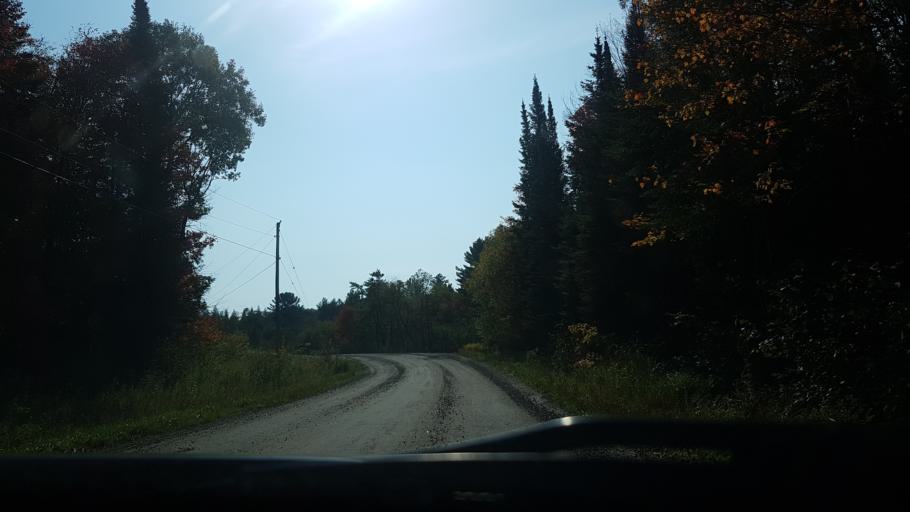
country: CA
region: Ontario
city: Bracebridge
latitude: 44.9409
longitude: -79.2424
